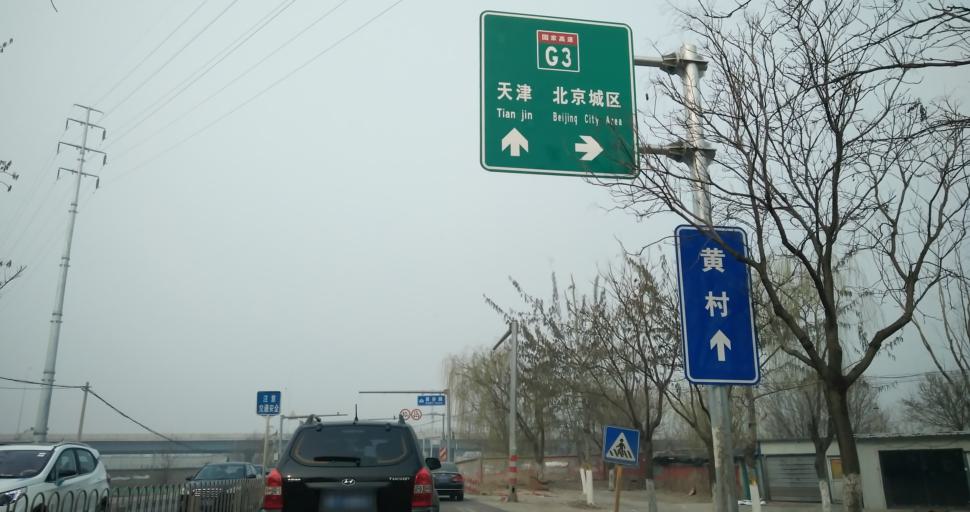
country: CN
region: Beijing
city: Yinghai
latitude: 39.7648
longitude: 116.4272
